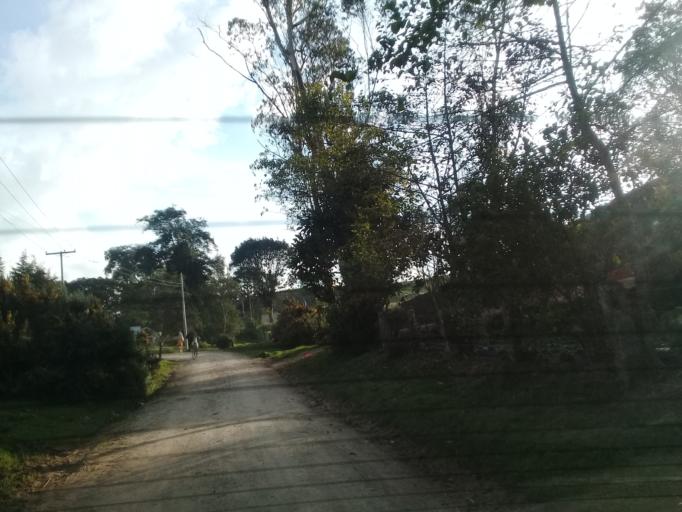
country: CO
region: Cundinamarca
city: Sibate
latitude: 4.4416
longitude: -74.2796
